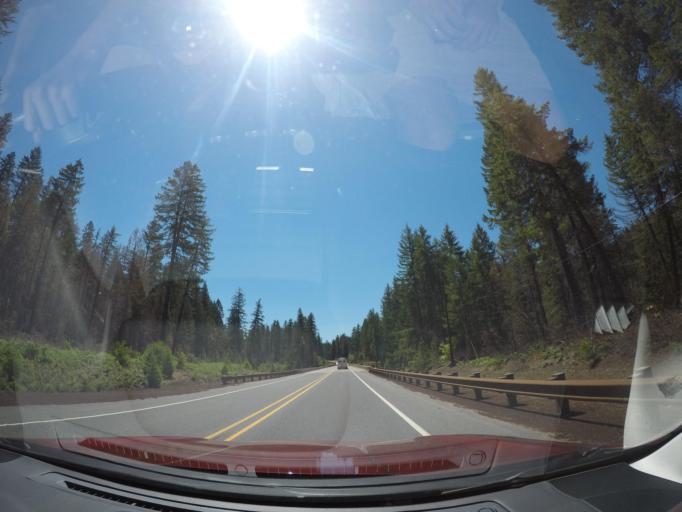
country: US
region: Oregon
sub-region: Linn County
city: Mill City
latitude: 44.6903
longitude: -121.9718
